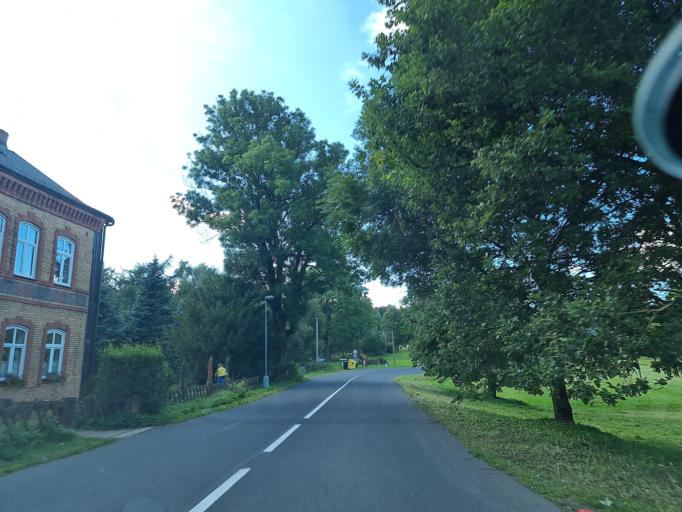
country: CZ
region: Ustecky
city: Mezibori
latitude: 50.6300
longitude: 13.5603
